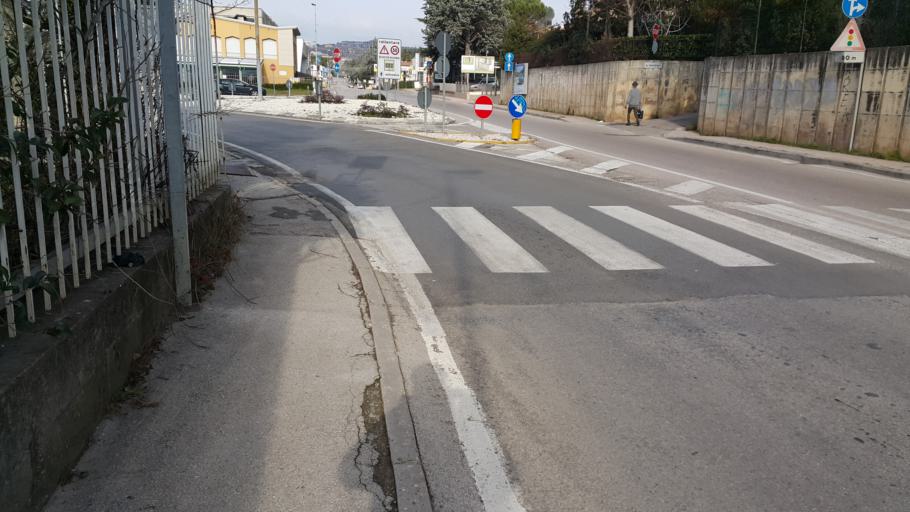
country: IT
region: Umbria
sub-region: Provincia di Perugia
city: Perugia
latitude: 43.0895
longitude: 12.3684
